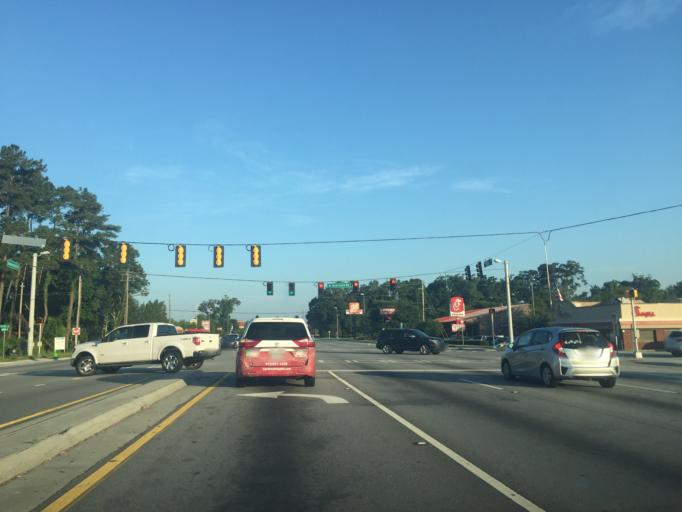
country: US
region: Georgia
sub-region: Chatham County
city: Montgomery
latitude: 31.9799
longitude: -81.1431
